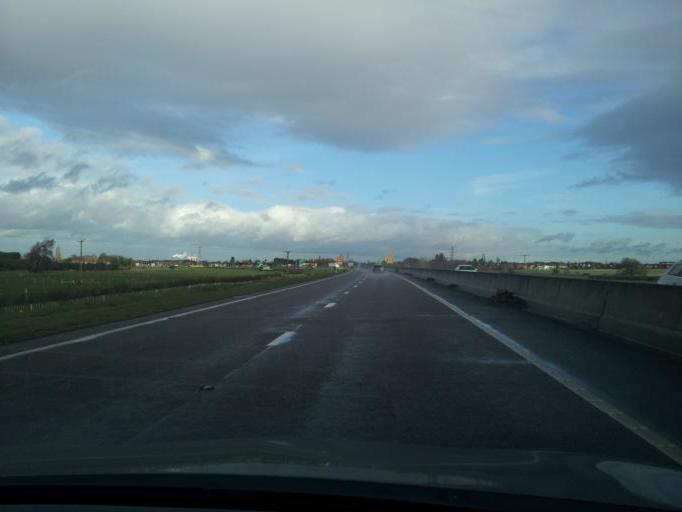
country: GB
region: England
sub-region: Nottinghamshire
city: Farndon
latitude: 53.0562
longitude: -0.8422
